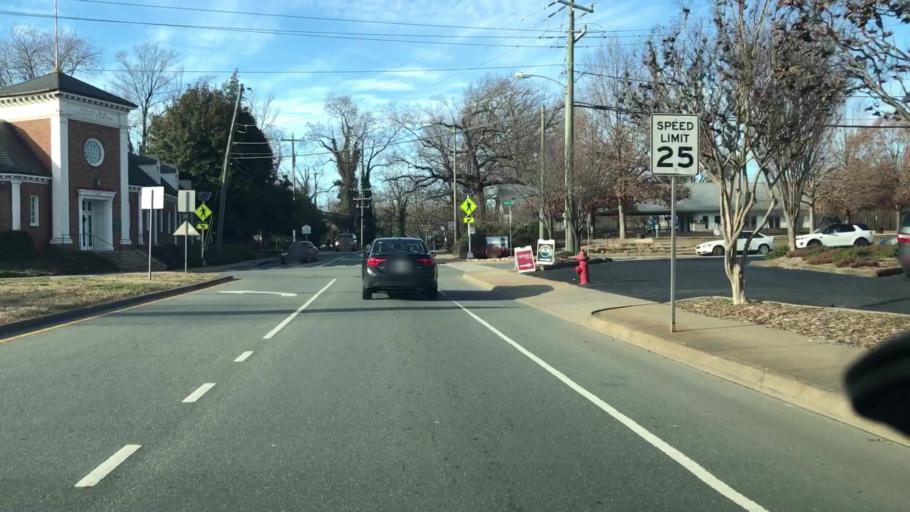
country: US
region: Virginia
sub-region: City of Charlottesville
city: Charlottesville
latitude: 38.0390
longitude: -78.4909
